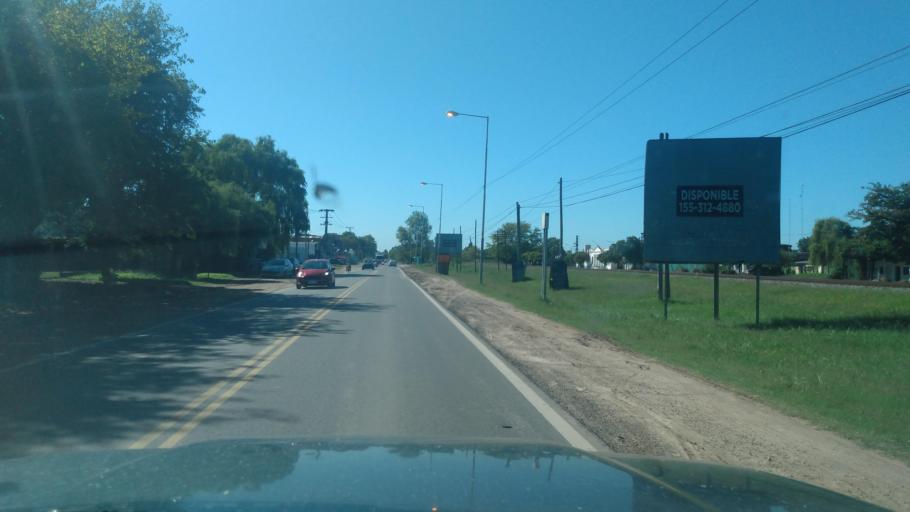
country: AR
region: Buenos Aires
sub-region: Partido de General Rodriguez
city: General Rodriguez
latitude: -34.6052
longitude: -58.9678
